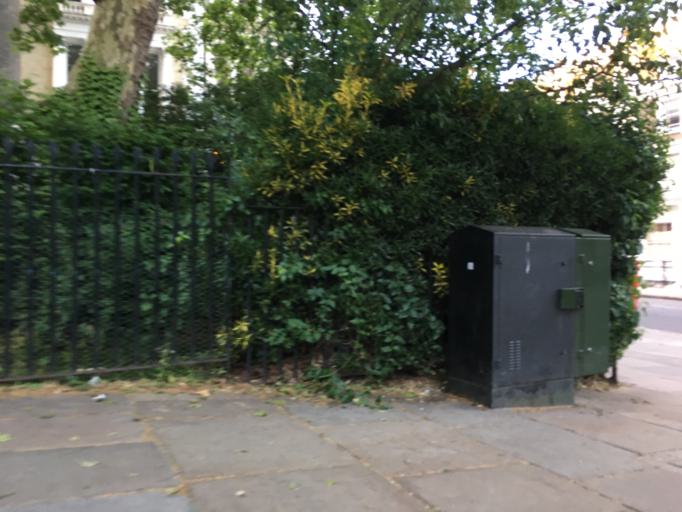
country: GB
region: England
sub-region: Greater London
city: Camden Town
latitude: 51.5403
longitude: -0.1578
